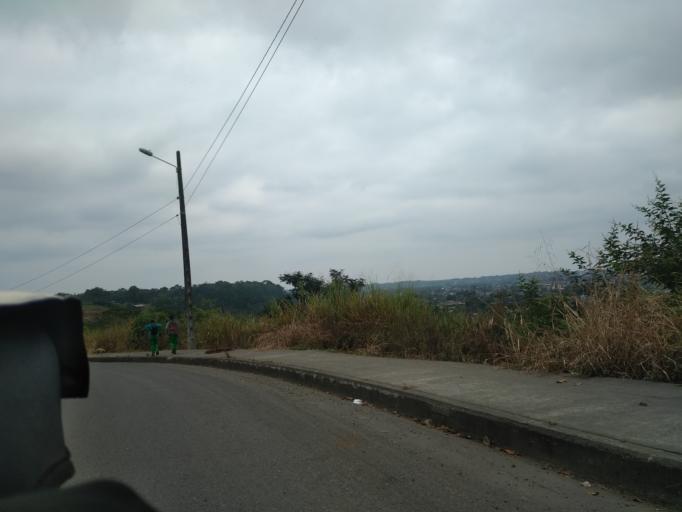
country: EC
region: Los Rios
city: Quevedo
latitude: -1.0264
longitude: -79.4423
